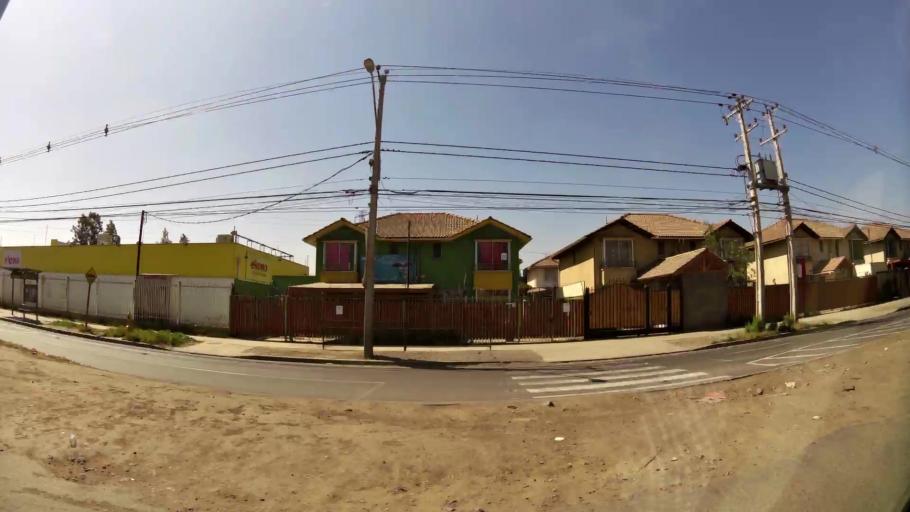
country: CL
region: Santiago Metropolitan
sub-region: Provincia de Santiago
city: Lo Prado
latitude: -33.3526
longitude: -70.7390
